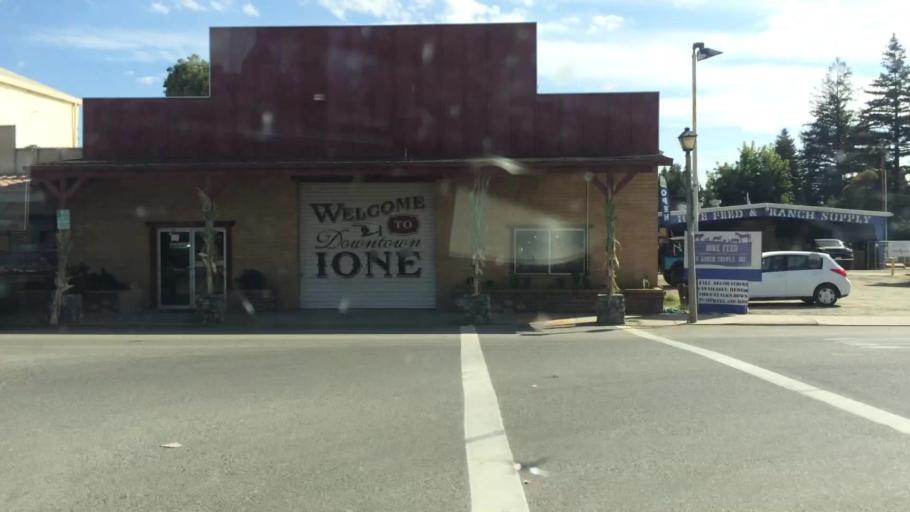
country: US
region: California
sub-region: Amador County
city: Ione
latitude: 38.3526
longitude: -120.9347
